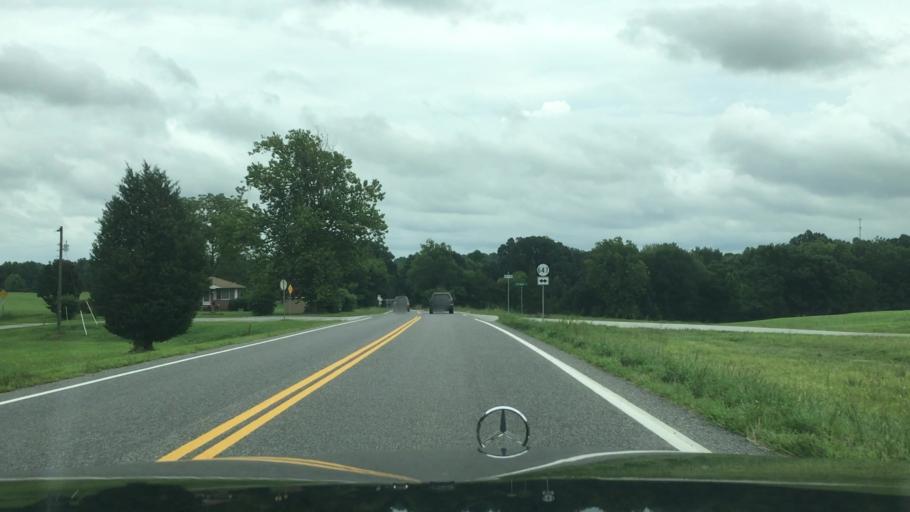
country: US
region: Virginia
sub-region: Nottoway County
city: Crewe
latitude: 37.2727
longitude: -78.1624
